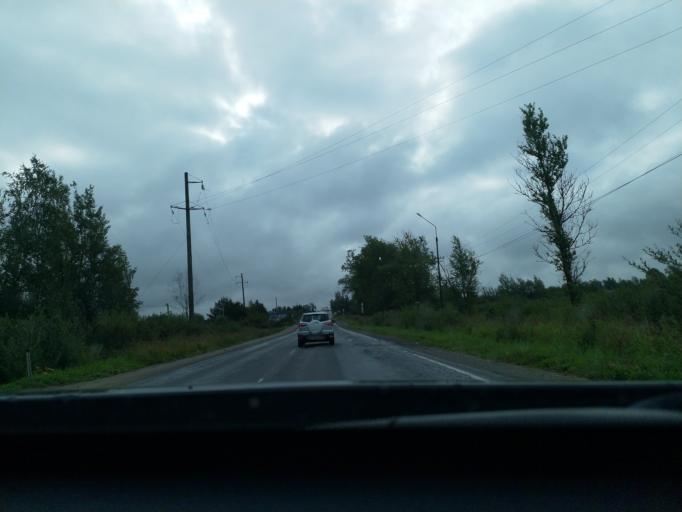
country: RU
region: Leningrad
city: Nikol'skoye
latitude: 59.6919
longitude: 30.8024
